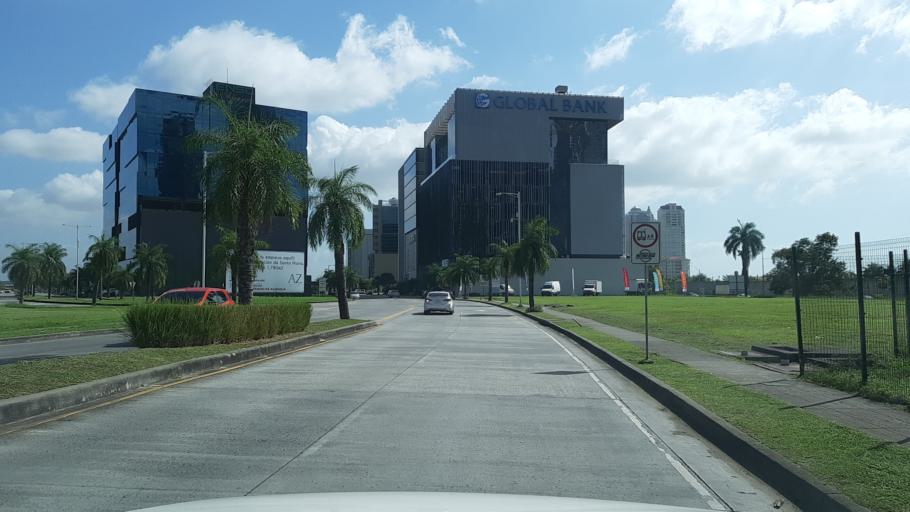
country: PA
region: Panama
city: San Miguelito
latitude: 9.0278
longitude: -79.4640
